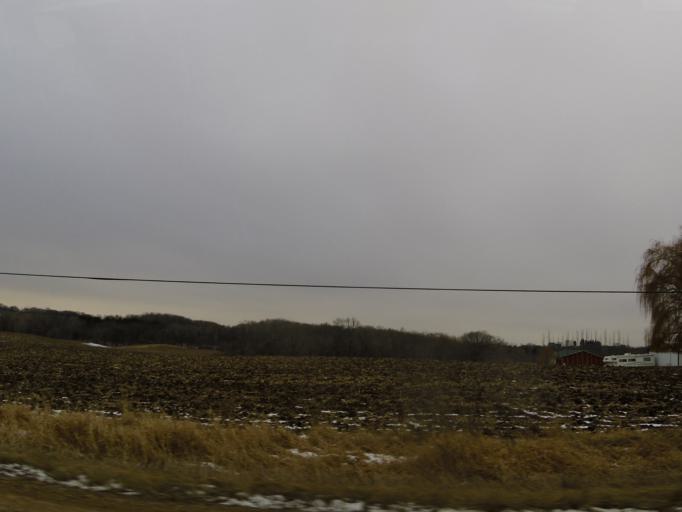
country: US
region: Minnesota
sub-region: Carver County
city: Carver
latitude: 44.7761
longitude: -93.6722
